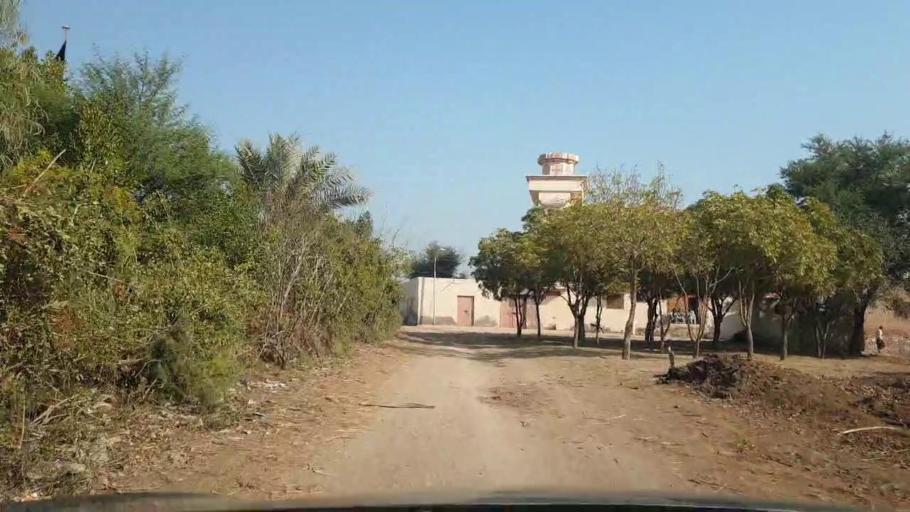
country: PK
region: Sindh
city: Tando Allahyar
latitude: 25.5101
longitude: 68.7256
